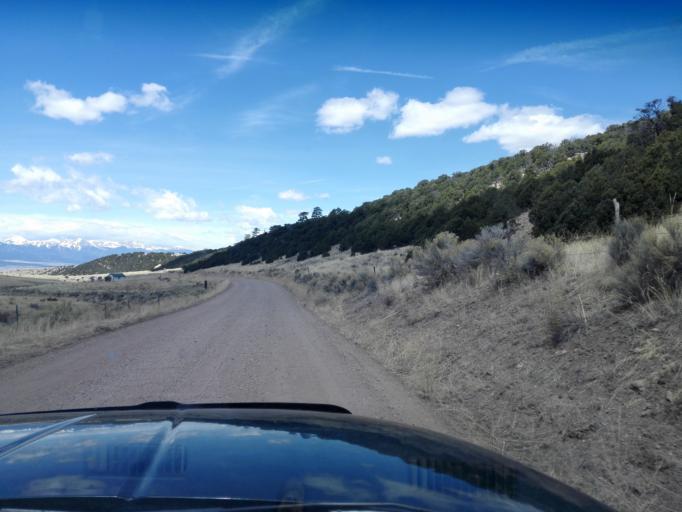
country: US
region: Colorado
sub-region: Custer County
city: Westcliffe
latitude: 37.9797
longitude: -105.2981
